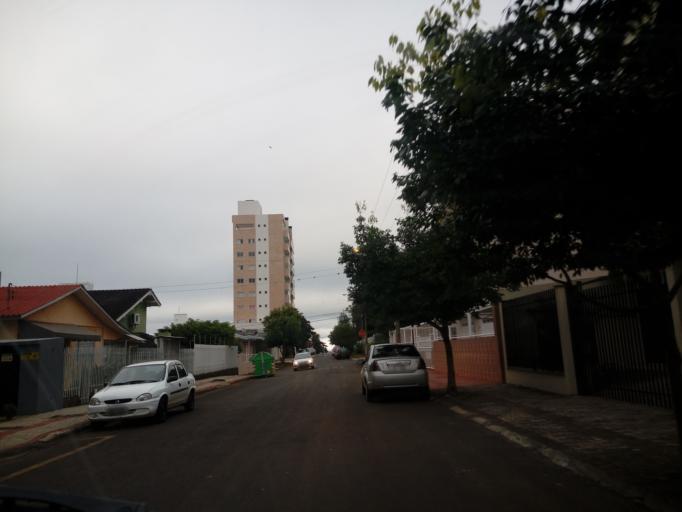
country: BR
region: Santa Catarina
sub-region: Chapeco
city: Chapeco
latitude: -27.0931
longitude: -52.6297
